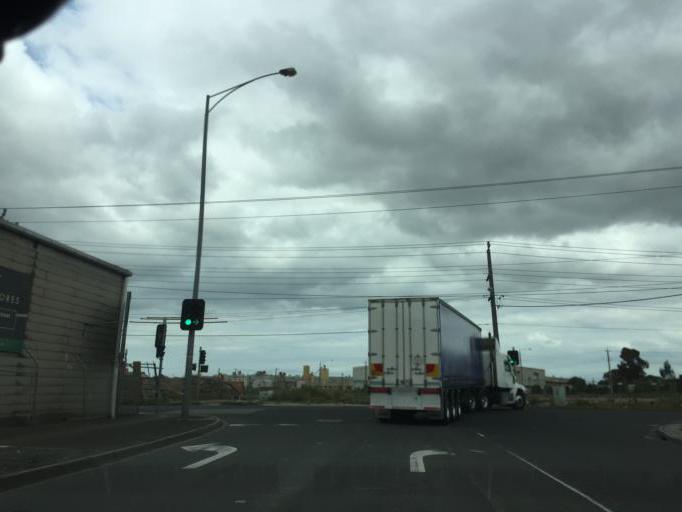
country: AU
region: Victoria
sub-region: Brimbank
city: Brooklyn
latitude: -37.8088
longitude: 144.8516
